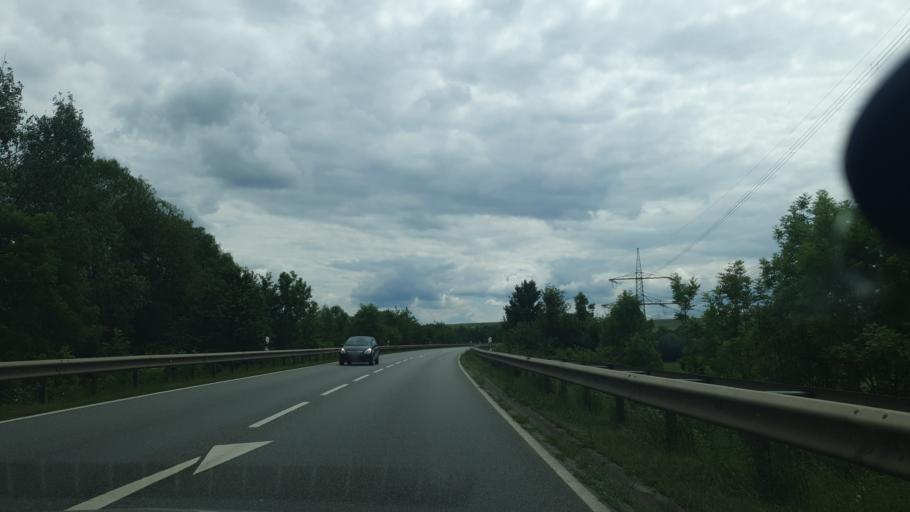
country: DE
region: Rheinland-Pfalz
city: Windesheim
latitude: 49.9076
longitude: 7.8236
